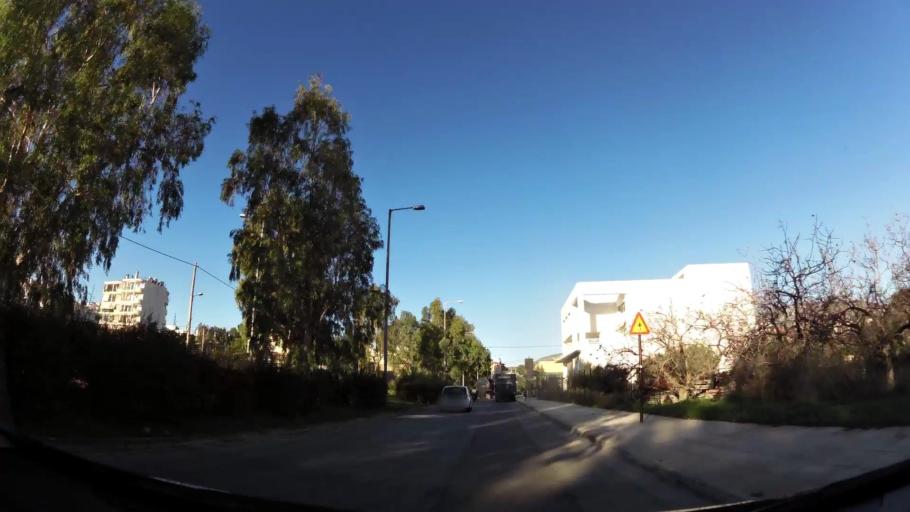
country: GR
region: Attica
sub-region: Nomarchia Anatolikis Attikis
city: Koropi
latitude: 37.9057
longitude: 23.8788
